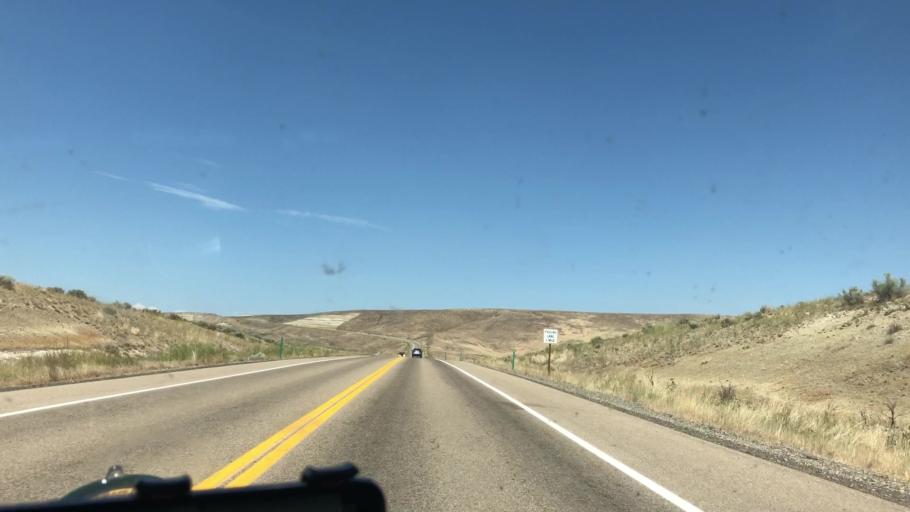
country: US
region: Idaho
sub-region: Owyhee County
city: Marsing
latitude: 43.2767
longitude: -116.9971
